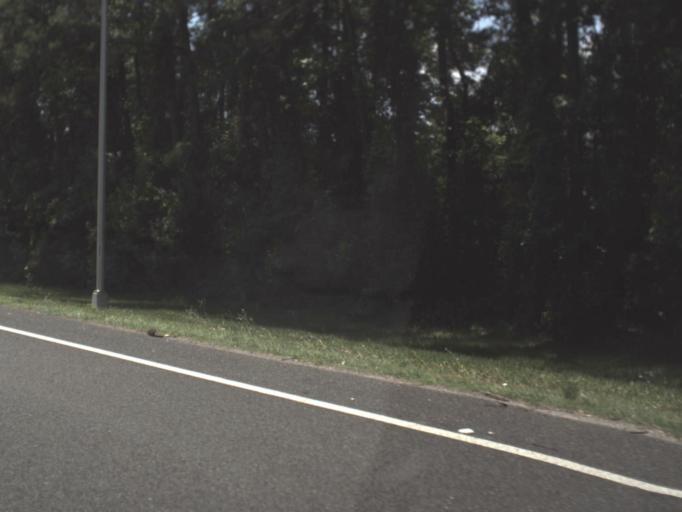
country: US
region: Florida
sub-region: Nassau County
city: Nassau Village-Ratliff
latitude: 30.4331
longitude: -81.7279
